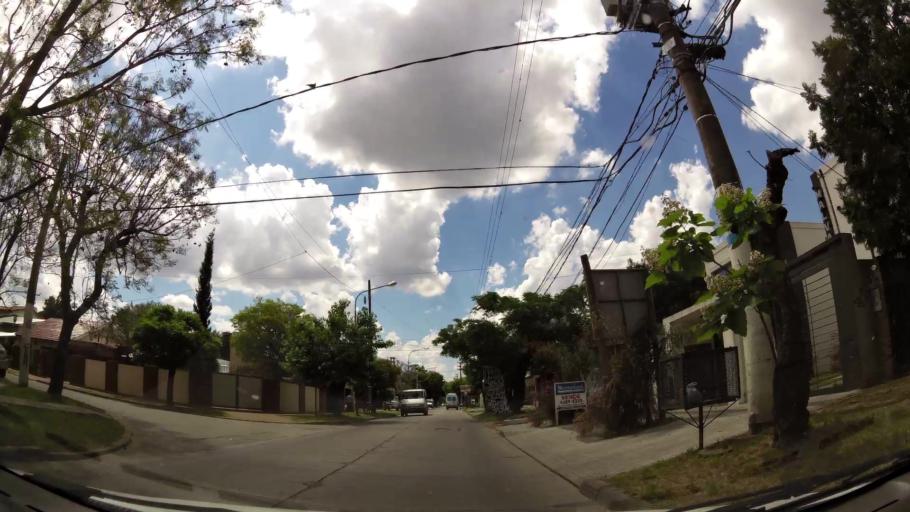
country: AR
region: Buenos Aires
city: Ituzaingo
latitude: -34.6527
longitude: -58.6755
